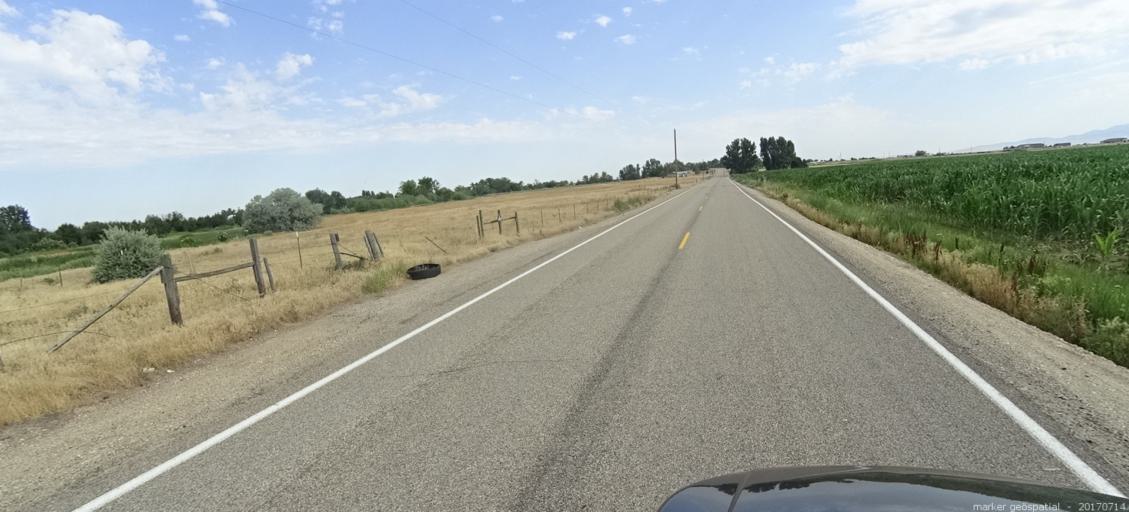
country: US
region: Idaho
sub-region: Ada County
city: Kuna
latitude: 43.4793
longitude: -116.3544
